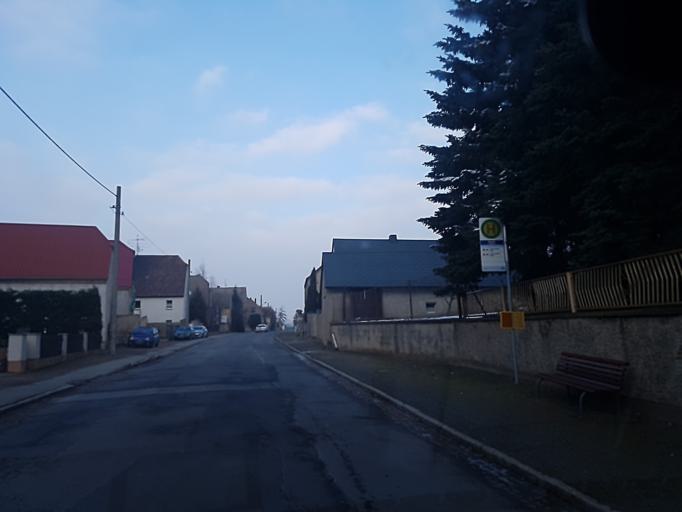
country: DE
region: Saxony
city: Oschatz
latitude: 51.3212
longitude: 13.0871
